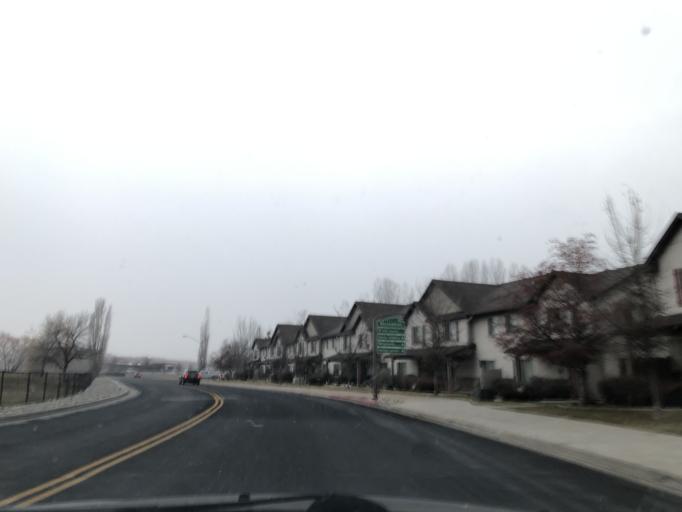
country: US
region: Utah
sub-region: Cache County
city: Logan
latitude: 41.7149
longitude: -111.8464
